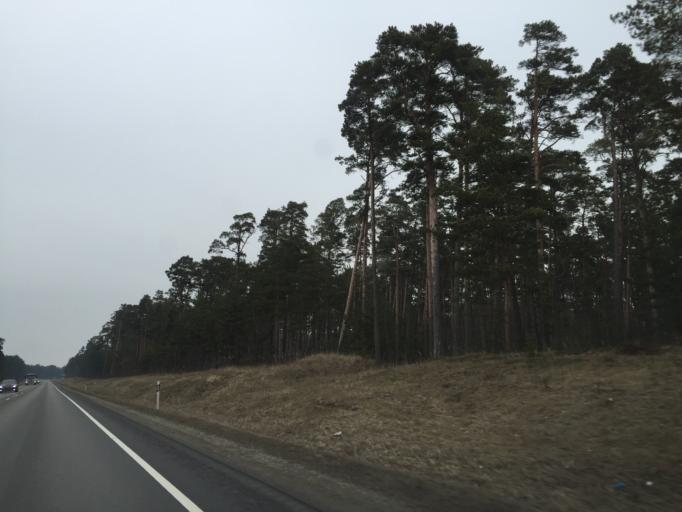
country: EE
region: Paernumaa
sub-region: Paernu linn
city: Parnu
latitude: 58.1930
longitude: 24.4898
